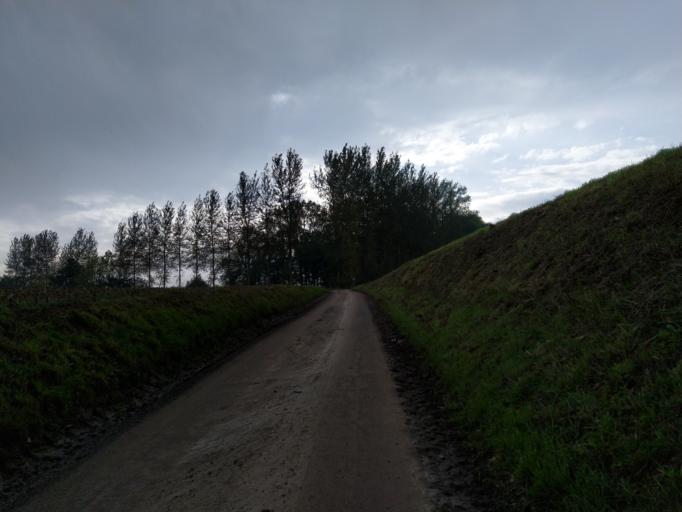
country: BE
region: Wallonia
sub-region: Province du Hainaut
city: Brugelette
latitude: 50.6133
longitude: 3.8773
